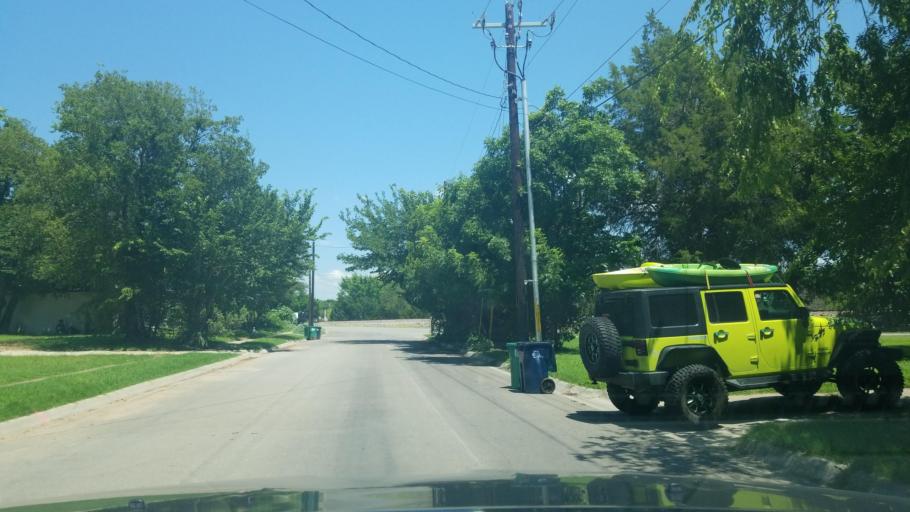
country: US
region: Texas
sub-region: Denton County
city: Denton
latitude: 33.2223
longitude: -97.1245
